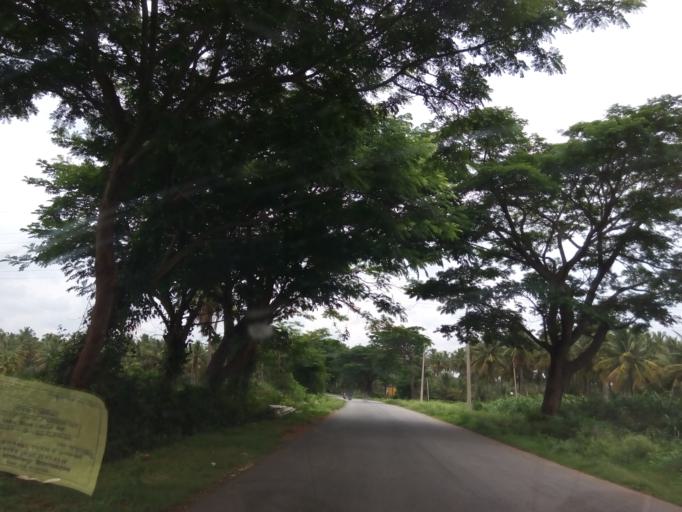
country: IN
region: Karnataka
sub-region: Hassan
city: Shravanabelagola
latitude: 12.8687
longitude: 76.4575
